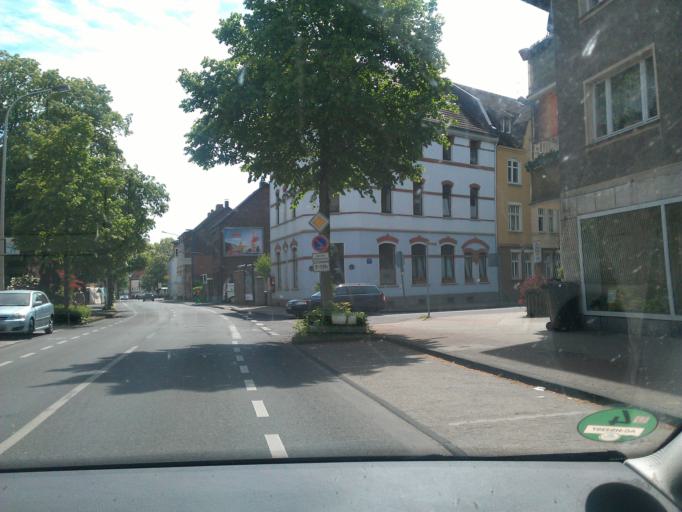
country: DE
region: North Rhine-Westphalia
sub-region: Regierungsbezirk Dusseldorf
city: Hilden
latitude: 51.1677
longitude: 6.9395
